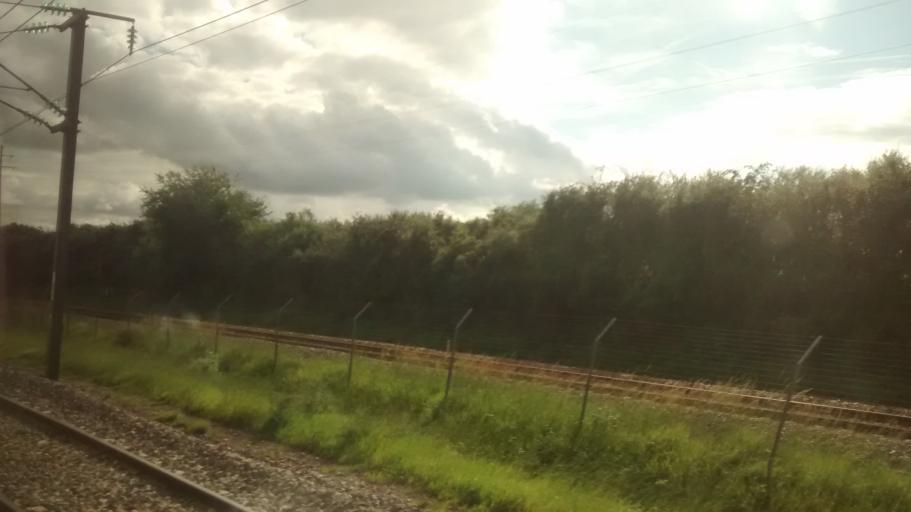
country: FR
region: Centre
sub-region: Departement d'Eure-et-Loir
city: Beville-le-Comte
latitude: 48.4084
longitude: 1.7472
